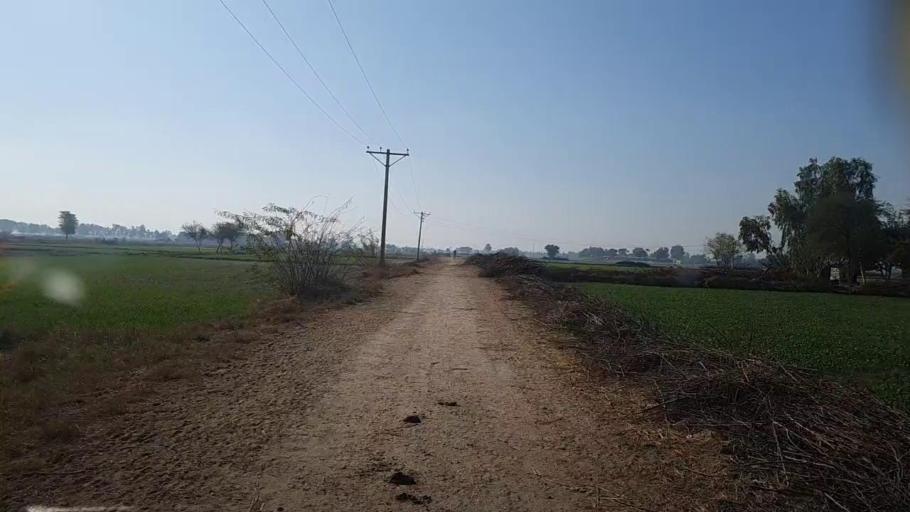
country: PK
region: Sindh
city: Khairpur
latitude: 27.9316
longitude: 69.6955
